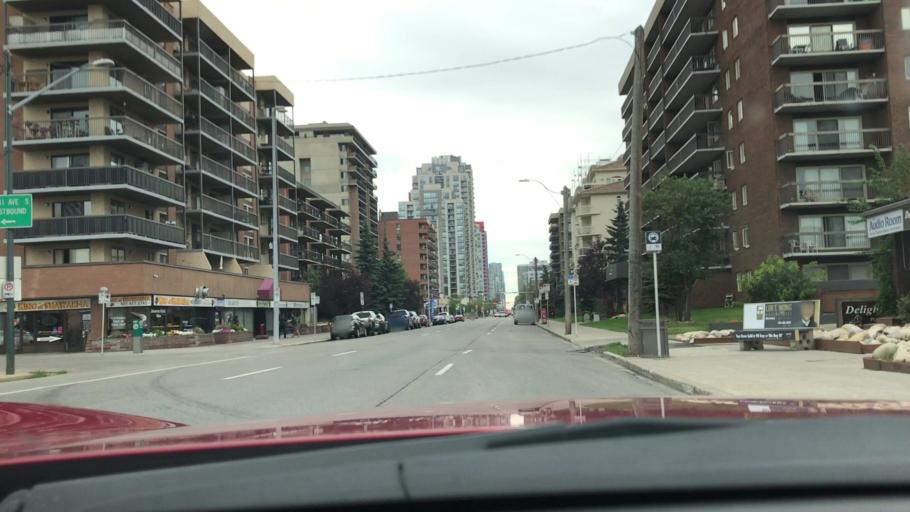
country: CA
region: Alberta
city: Calgary
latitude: 51.0423
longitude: -114.0944
